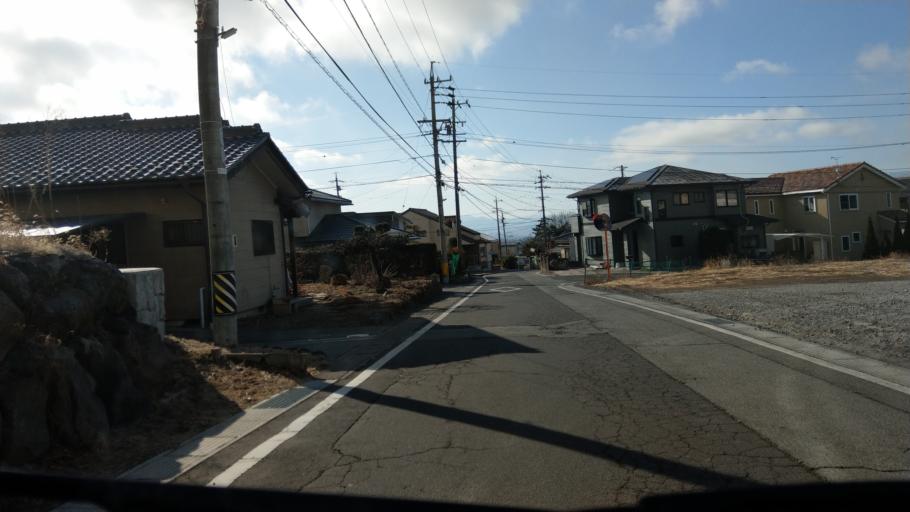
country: JP
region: Nagano
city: Komoro
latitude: 36.3274
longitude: 138.4464
